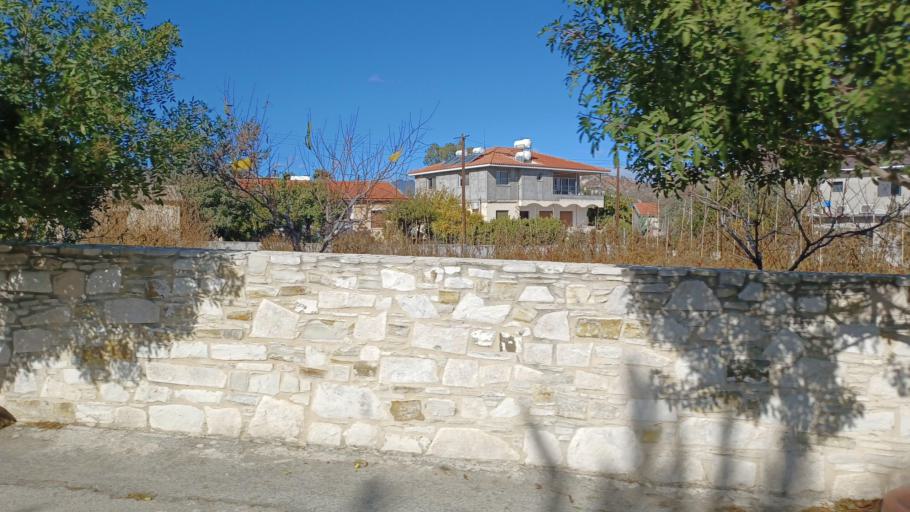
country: CY
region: Limassol
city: Pyrgos
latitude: 34.7783
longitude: 33.2541
